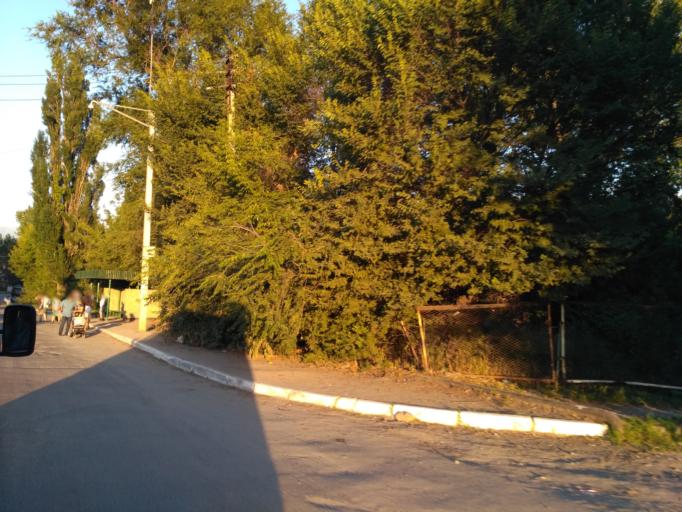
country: KZ
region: Almaty Qalasy
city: Almaty
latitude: 43.1775
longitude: 76.7557
